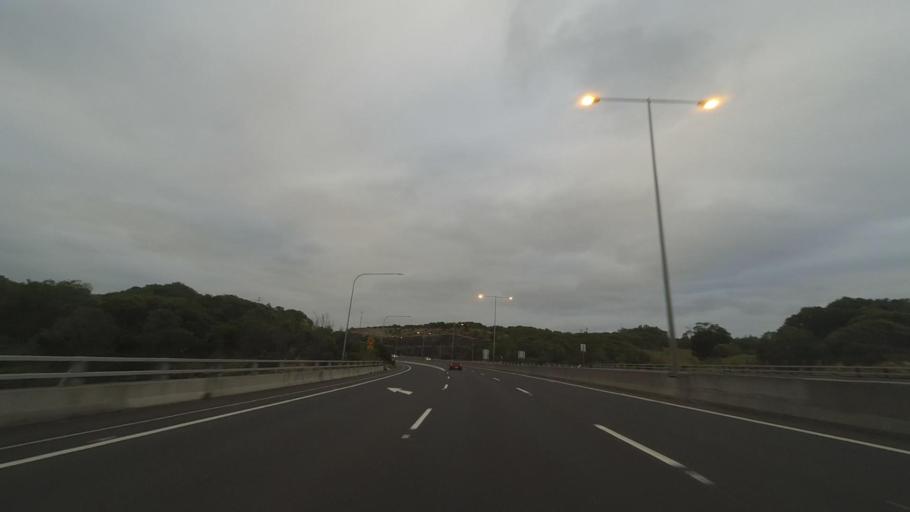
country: AU
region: New South Wales
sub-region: Kiama
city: Kiama
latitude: -34.6515
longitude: 150.8537
